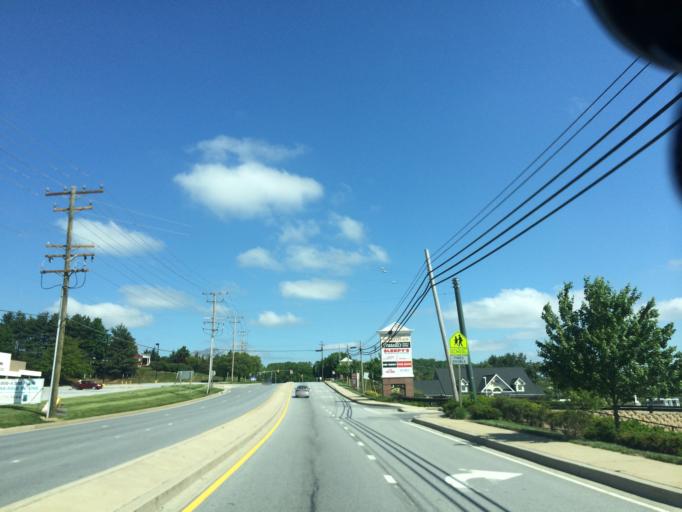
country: US
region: Maryland
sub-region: Carroll County
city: Manchester
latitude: 39.6382
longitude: -76.8672
